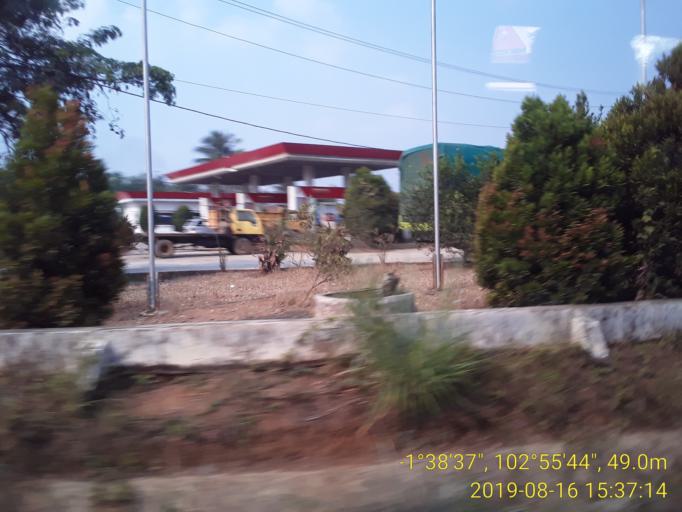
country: ID
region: Jambi
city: Mersam
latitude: -1.6439
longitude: 102.9290
